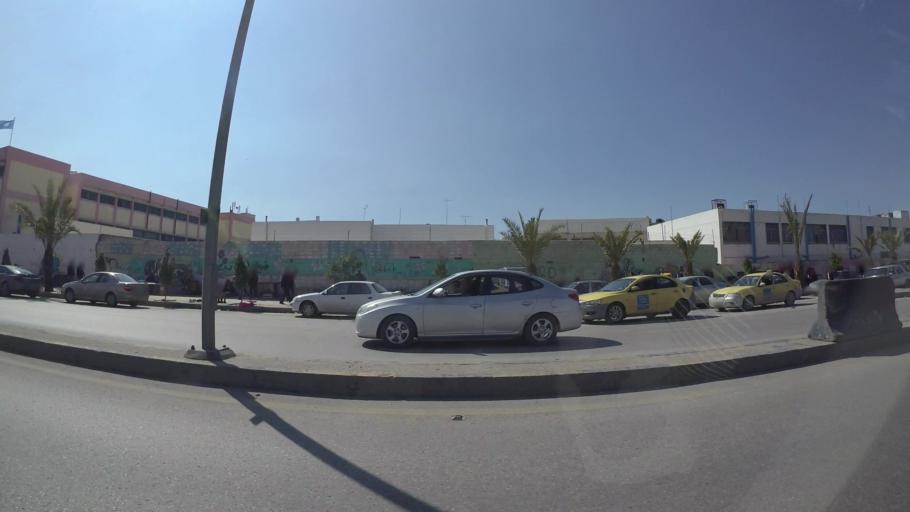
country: JO
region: Zarqa
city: Zarqa
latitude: 32.0592
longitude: 36.0944
